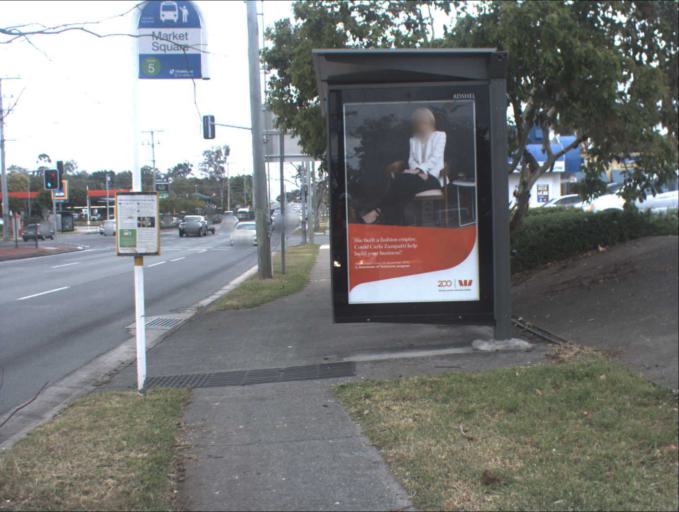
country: AU
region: Queensland
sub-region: Logan
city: Logan City
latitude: -27.6436
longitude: 153.1184
